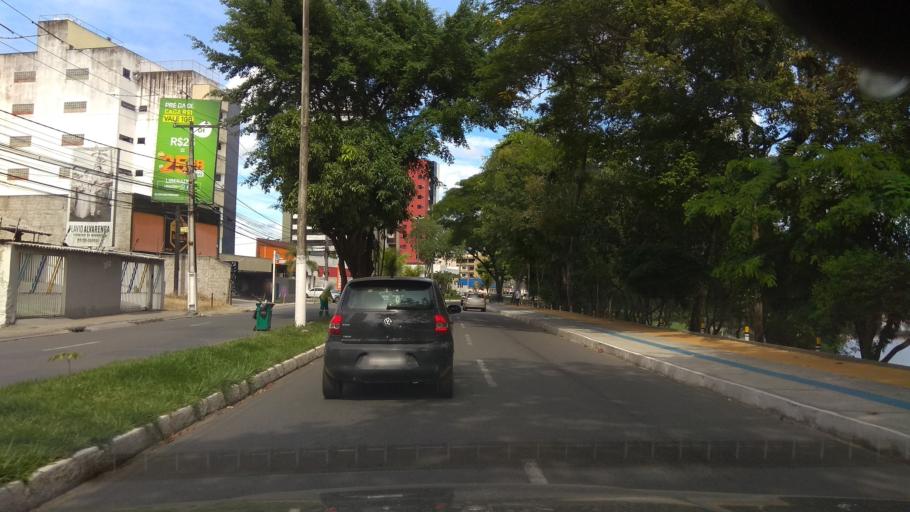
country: BR
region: Bahia
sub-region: Itabuna
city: Itabuna
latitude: -14.7978
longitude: -39.2753
